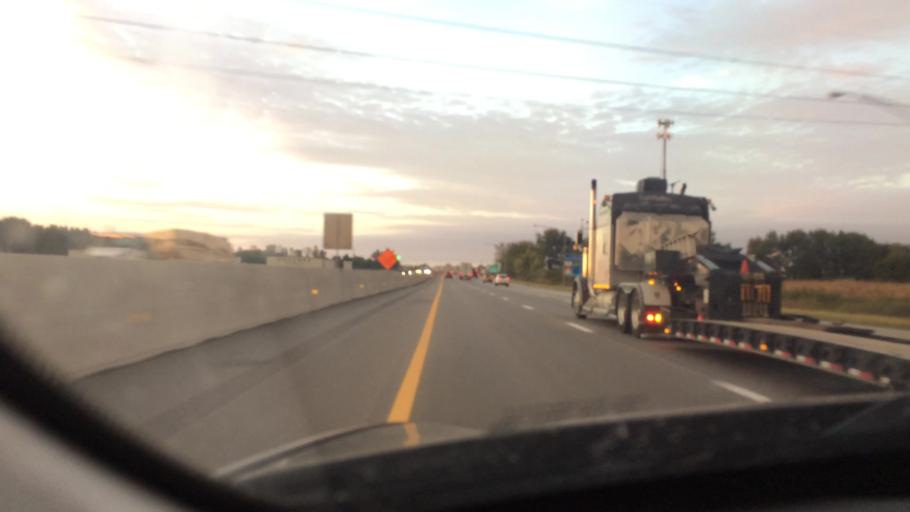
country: US
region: Ohio
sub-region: Hancock County
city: Findlay
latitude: 41.0983
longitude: -83.6599
